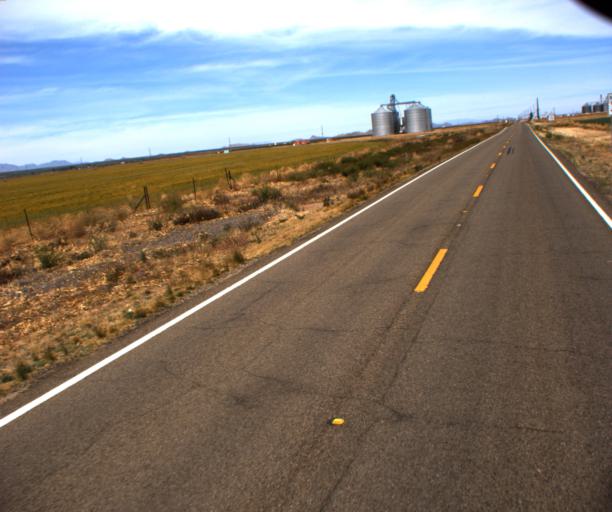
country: US
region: Arizona
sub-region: Cochise County
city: Tombstone
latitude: 31.7532
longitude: -109.6890
